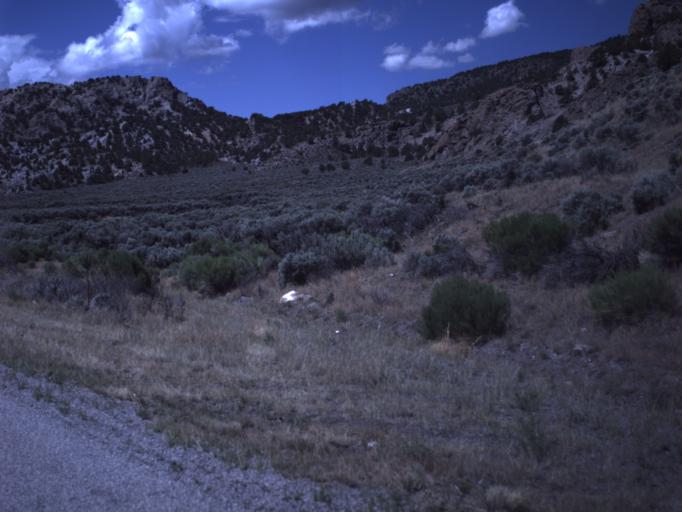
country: US
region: Utah
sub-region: Piute County
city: Junction
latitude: 38.0555
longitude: -112.3501
